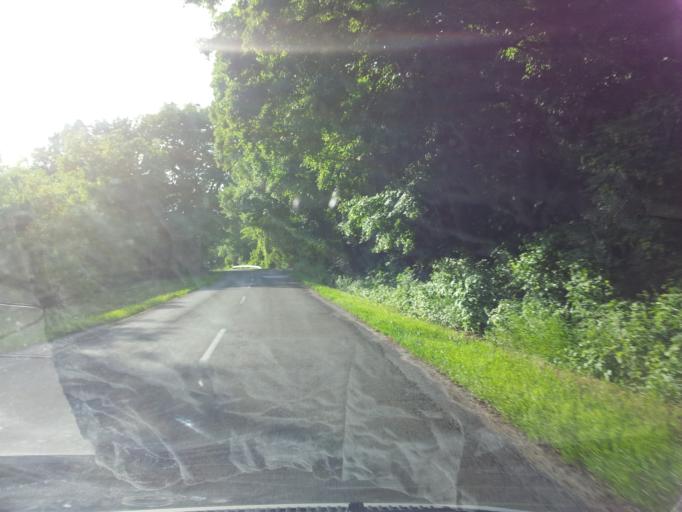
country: HU
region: Komarom-Esztergom
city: Kesztolc
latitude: 47.7444
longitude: 18.8055
